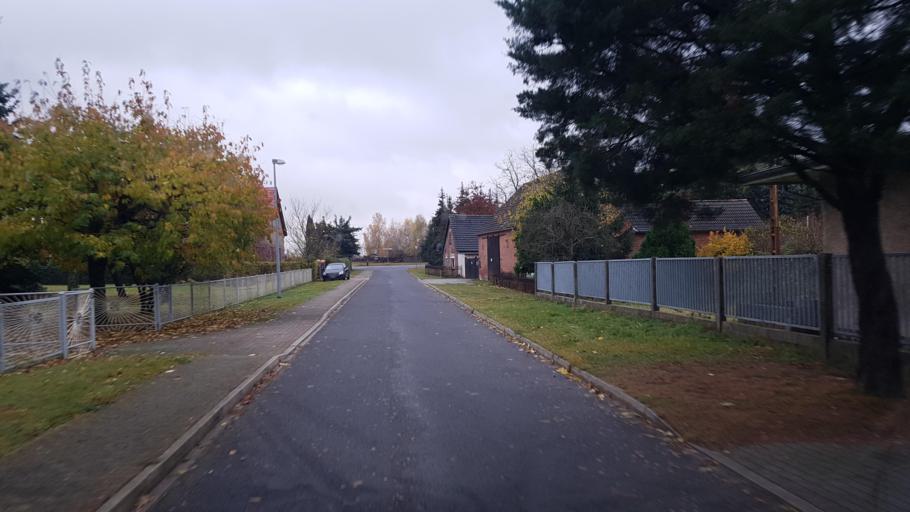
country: DE
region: Brandenburg
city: Drebkau
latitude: 51.6625
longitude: 14.2510
